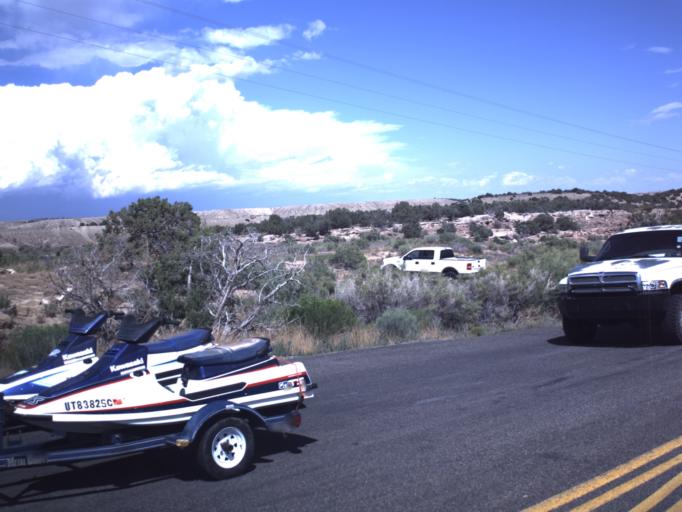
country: US
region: Utah
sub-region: Duchesne County
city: Duchesne
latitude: 40.1778
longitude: -110.4524
